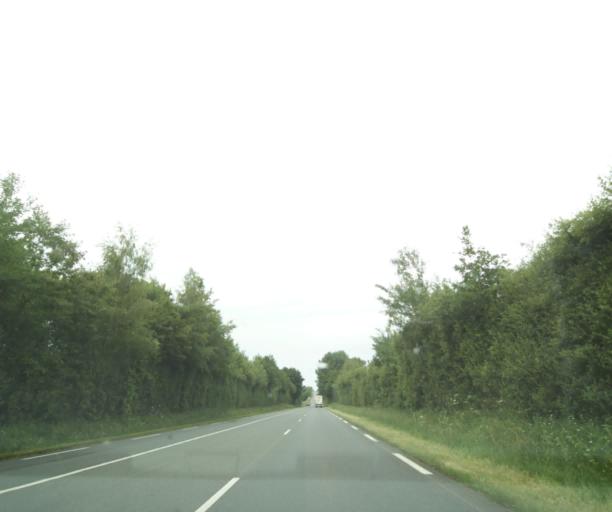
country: FR
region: Poitou-Charentes
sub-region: Departement des Deux-Sevres
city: Saint-Pardoux
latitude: 46.5617
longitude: -0.3032
